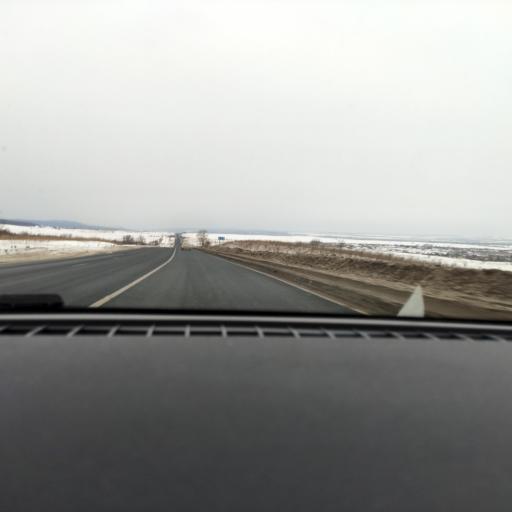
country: RU
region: Samara
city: Novosemeykino
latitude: 53.3985
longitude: 50.4202
